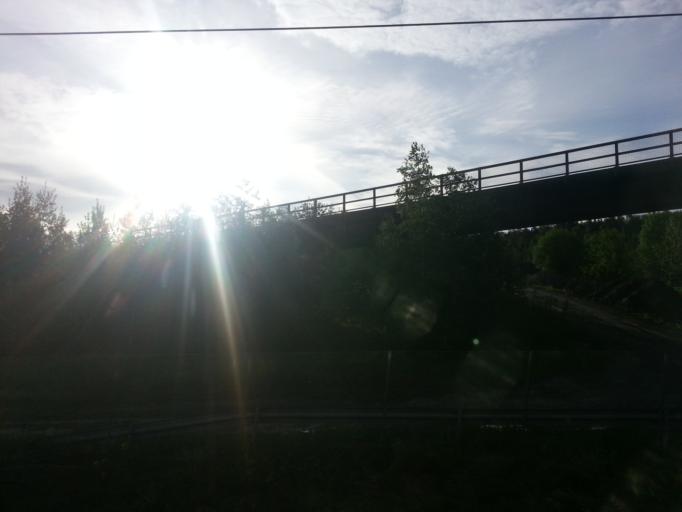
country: NO
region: Akershus
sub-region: Ullensaker
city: Jessheim
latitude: 60.1285
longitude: 11.1595
